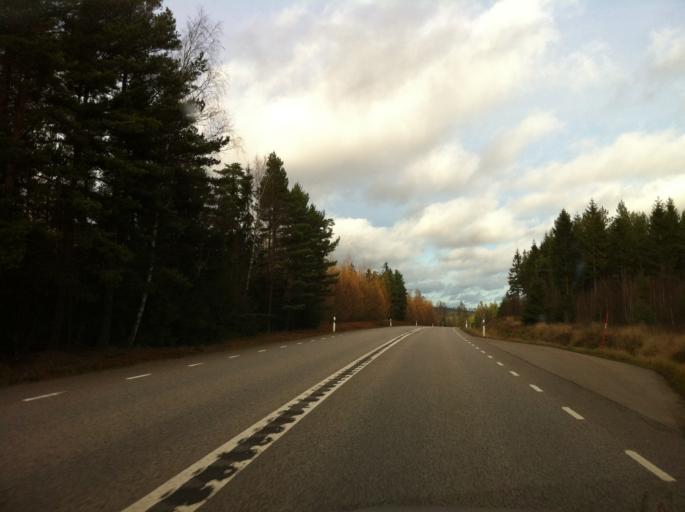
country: SE
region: Kronoberg
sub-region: Vaxjo Kommun
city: Braas
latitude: 57.0705
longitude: 15.1600
